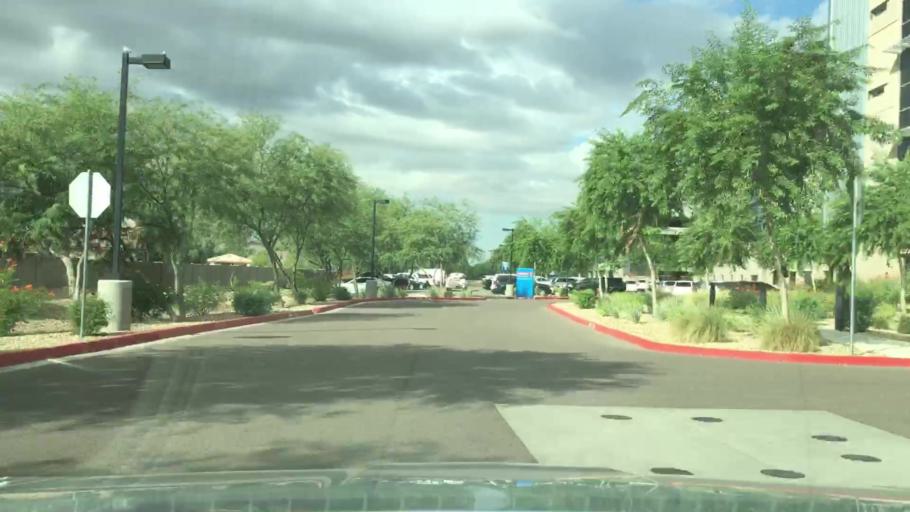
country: US
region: Arizona
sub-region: Maricopa County
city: Tolleson
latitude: 33.4772
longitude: -112.2569
